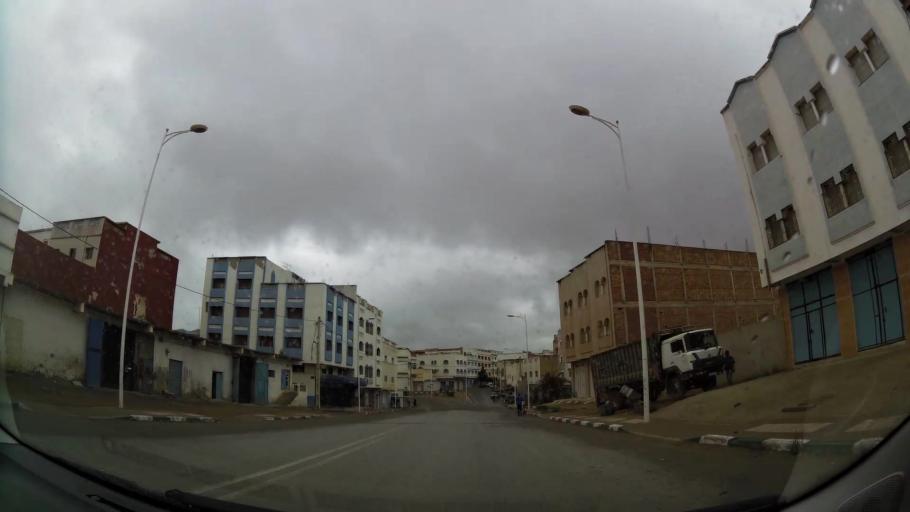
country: MA
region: Oriental
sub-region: Nador
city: Midar
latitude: 35.0479
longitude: -3.4516
